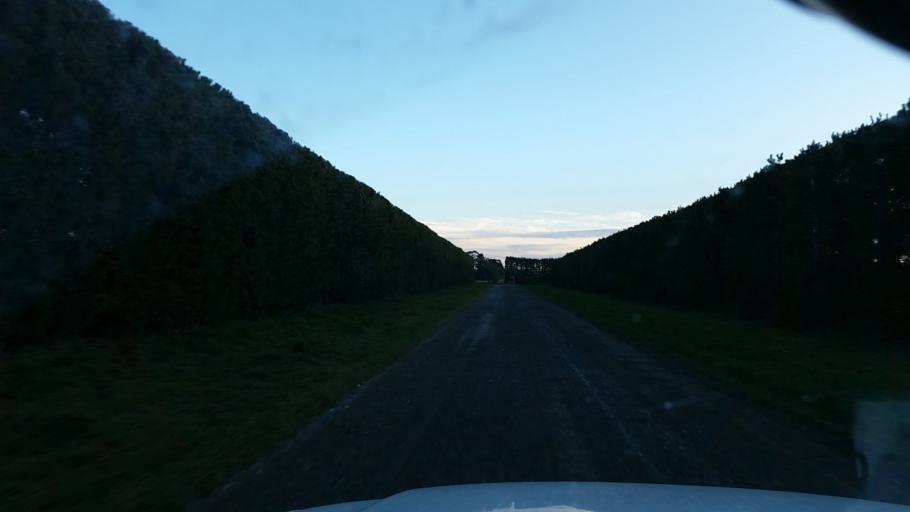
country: NZ
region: Canterbury
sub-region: Ashburton District
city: Tinwald
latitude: -43.9085
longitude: 171.5465
